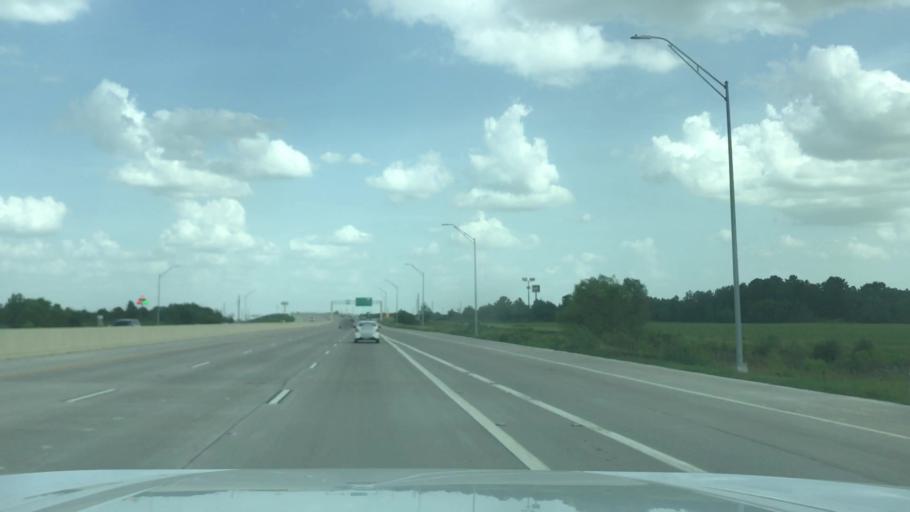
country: US
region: Texas
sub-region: Waller County
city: Waller
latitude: 30.0665
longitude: -95.9165
